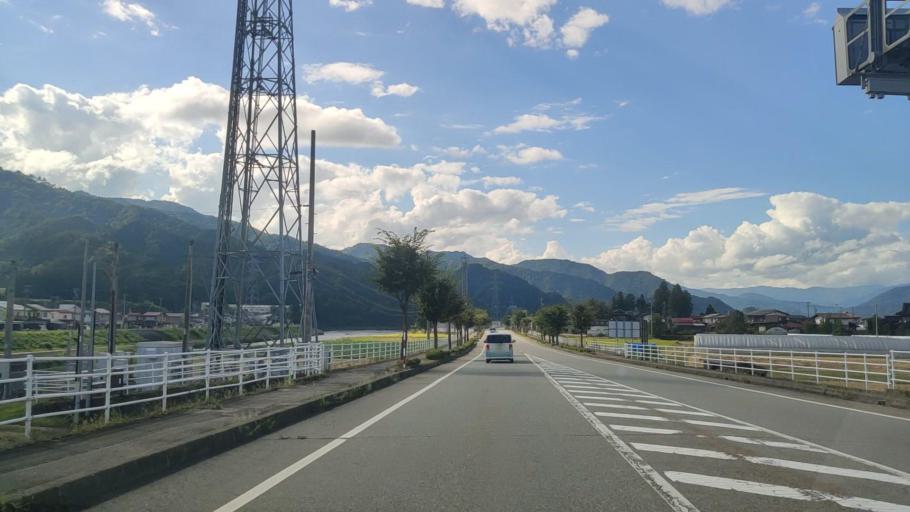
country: JP
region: Gifu
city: Takayama
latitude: 36.2173
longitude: 137.2004
